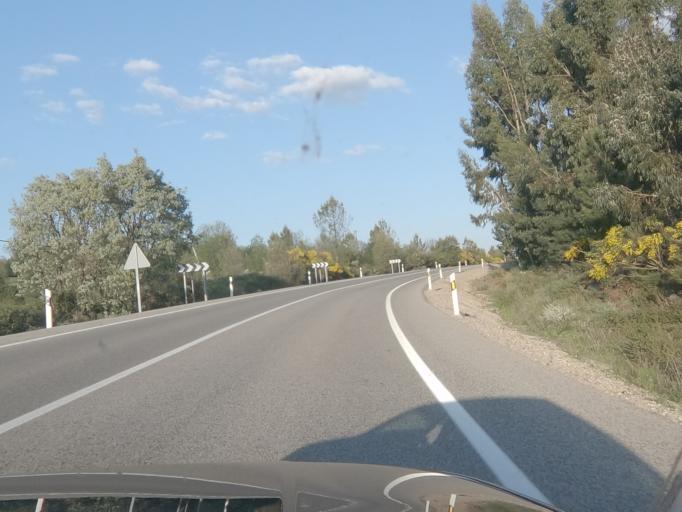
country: PT
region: Portalegre
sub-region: Portalegre
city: Sao Juliao
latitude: 39.3427
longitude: -7.2832
